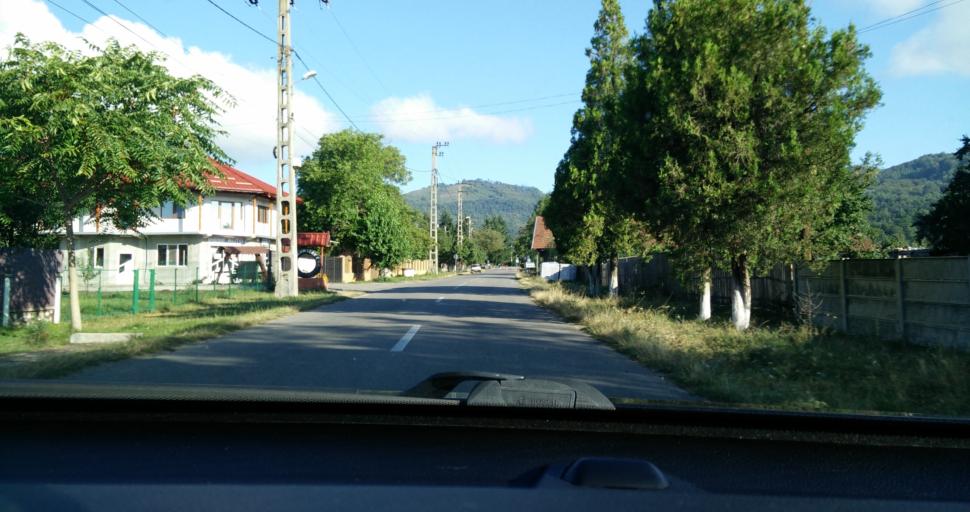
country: RO
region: Gorj
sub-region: Comuna Polovragi
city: Polovragi
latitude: 45.1752
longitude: 23.7999
